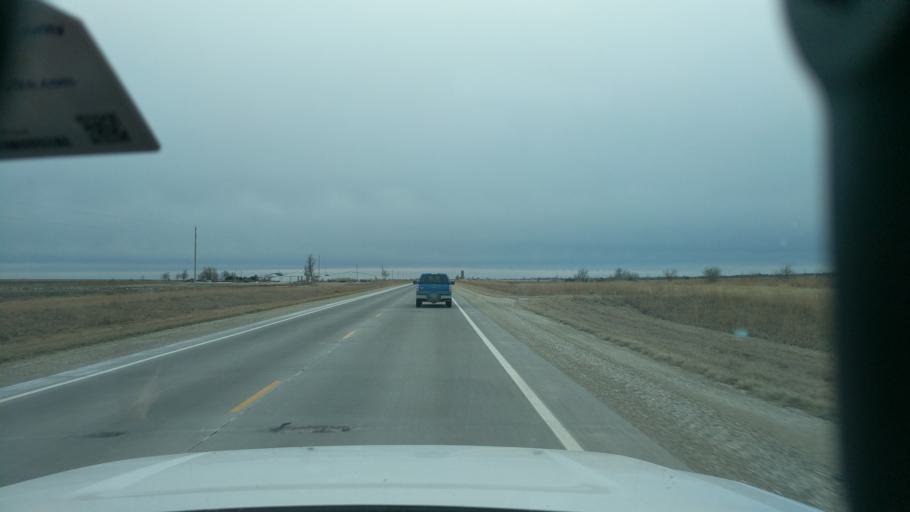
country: US
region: Kansas
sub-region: Dickinson County
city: Herington
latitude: 38.5894
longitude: -96.9482
